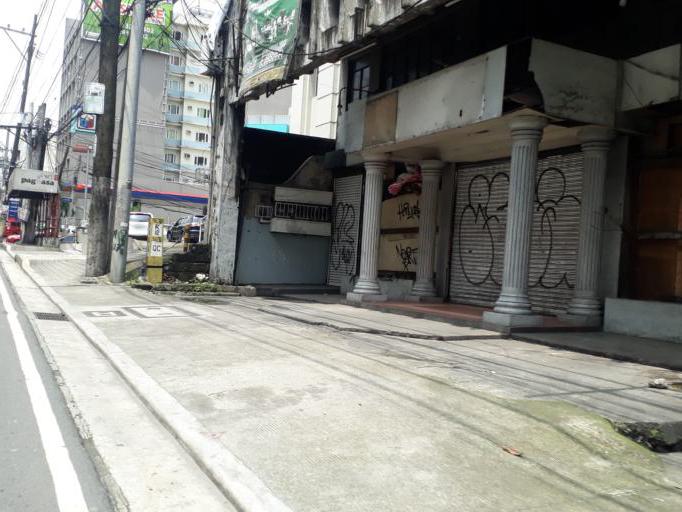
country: PH
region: Metro Manila
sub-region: Marikina
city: Calumpang
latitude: 14.6291
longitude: 121.0685
